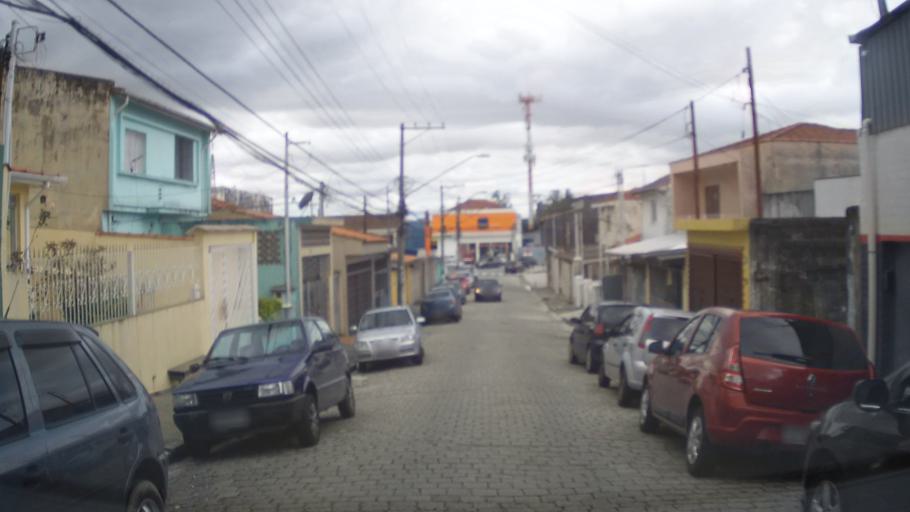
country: BR
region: Sao Paulo
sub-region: Guarulhos
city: Guarulhos
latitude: -23.4993
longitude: -46.5523
